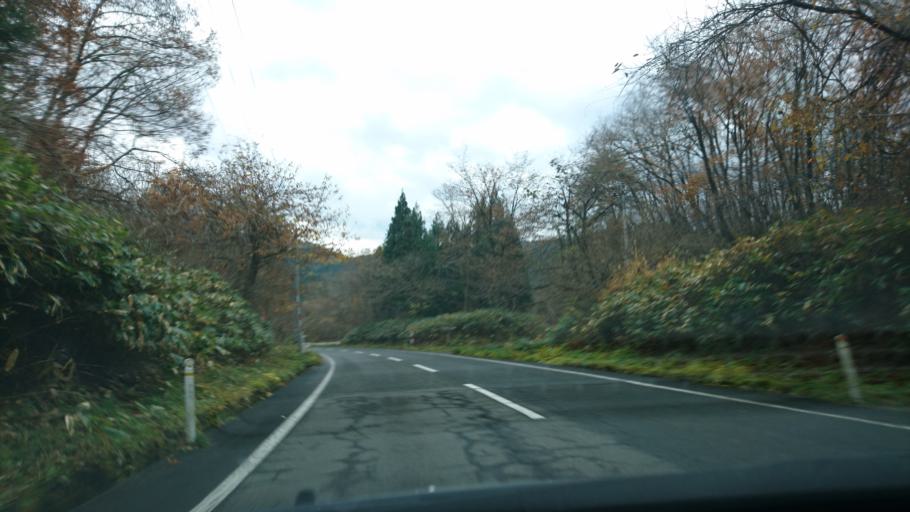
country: JP
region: Iwate
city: Ichinoseki
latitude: 38.8987
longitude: 140.9058
